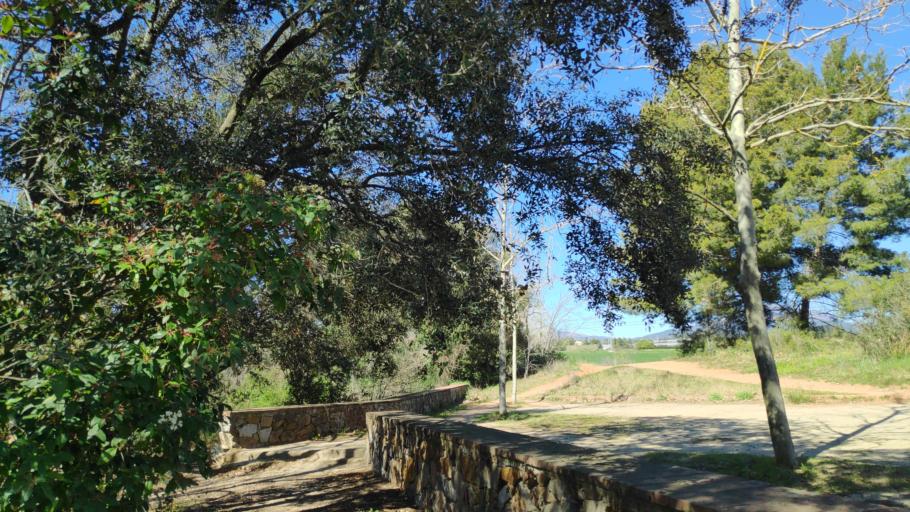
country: ES
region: Catalonia
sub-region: Provincia de Barcelona
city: Sant Quirze del Valles
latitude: 41.5640
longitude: 2.0724
